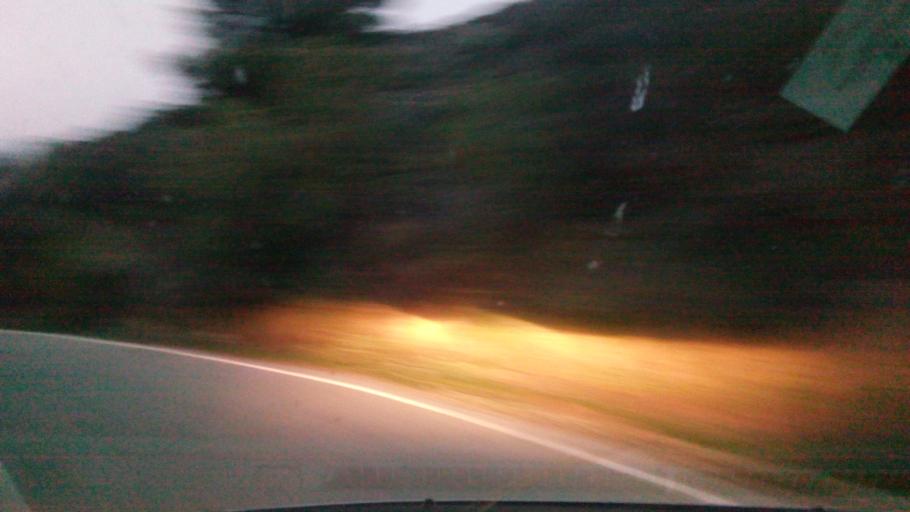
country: CY
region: Limassol
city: Kyperounta
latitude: 34.9052
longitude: 33.0885
